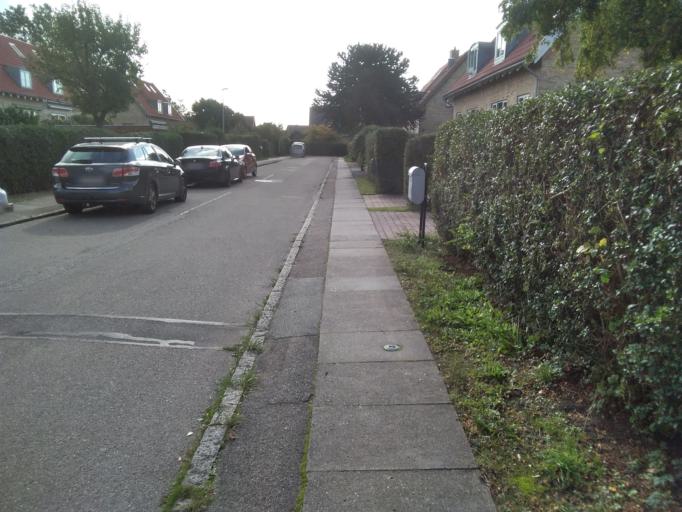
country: DK
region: Capital Region
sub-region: Tarnby Kommune
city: Tarnby
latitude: 55.6340
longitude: 12.6167
